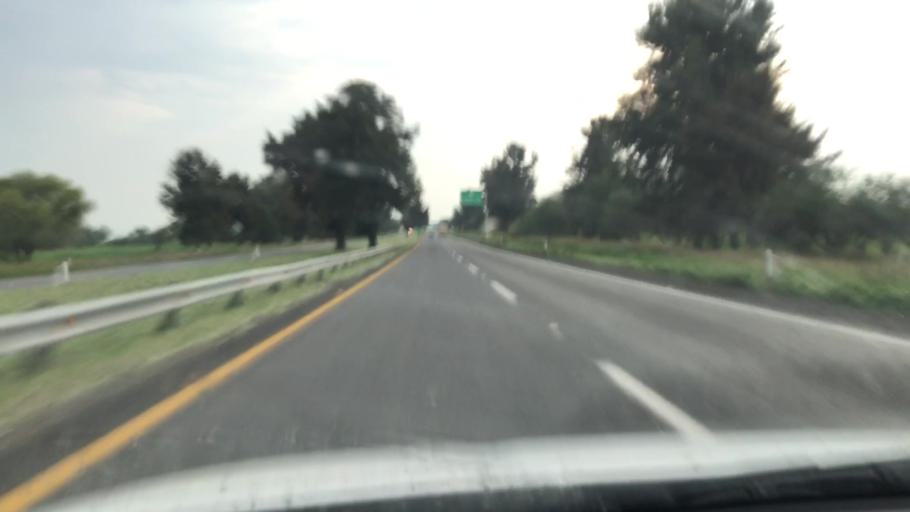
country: MX
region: Michoacan
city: Vistahermosa de Negrete
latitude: 20.2816
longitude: -102.4570
